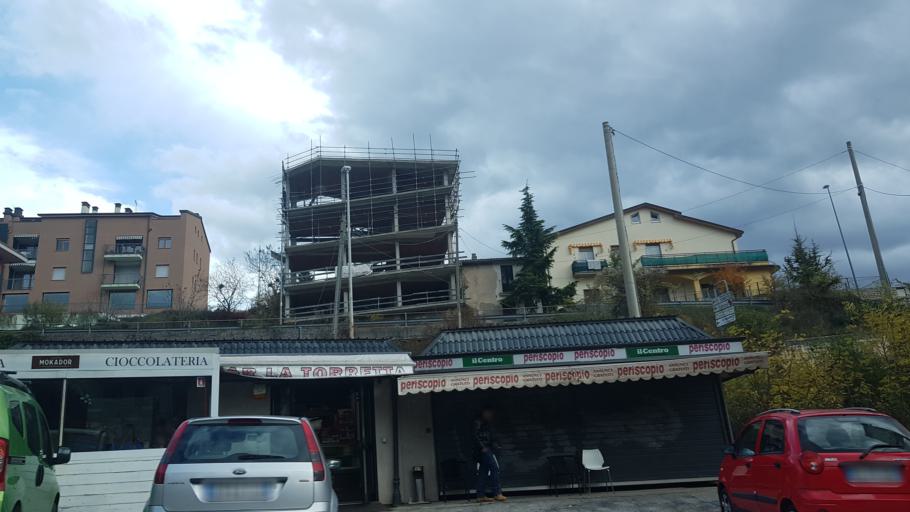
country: IT
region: Abruzzo
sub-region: Provincia dell' Aquila
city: L'Aquila
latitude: 42.3465
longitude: 13.4110
